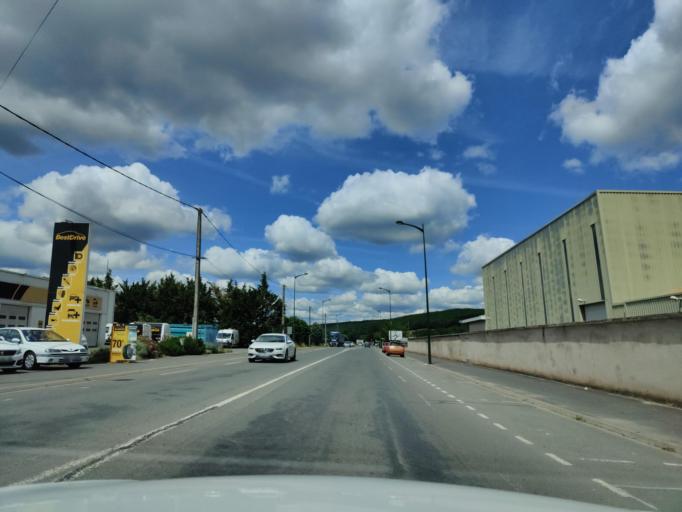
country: FR
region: Centre
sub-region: Departement du Cher
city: Orval
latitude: 46.7317
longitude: 2.4940
